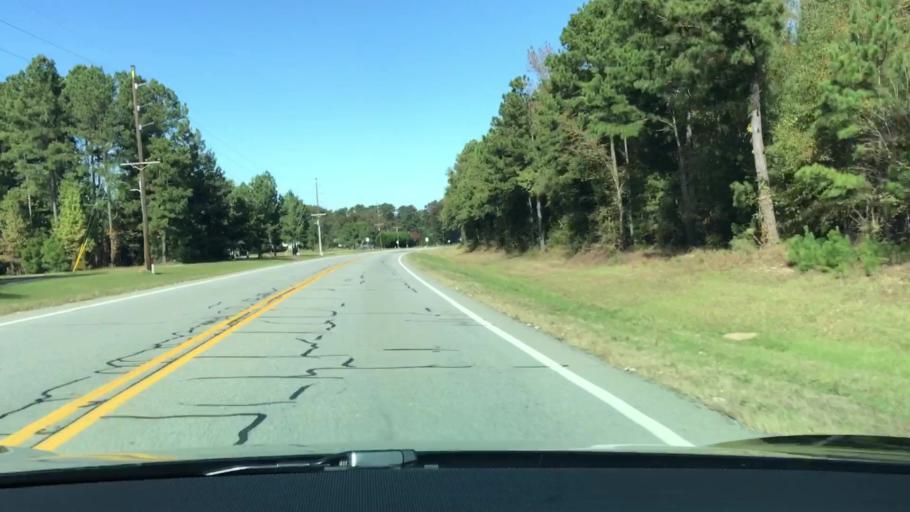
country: US
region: Georgia
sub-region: Warren County
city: Warrenton
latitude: 33.3917
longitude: -82.6473
